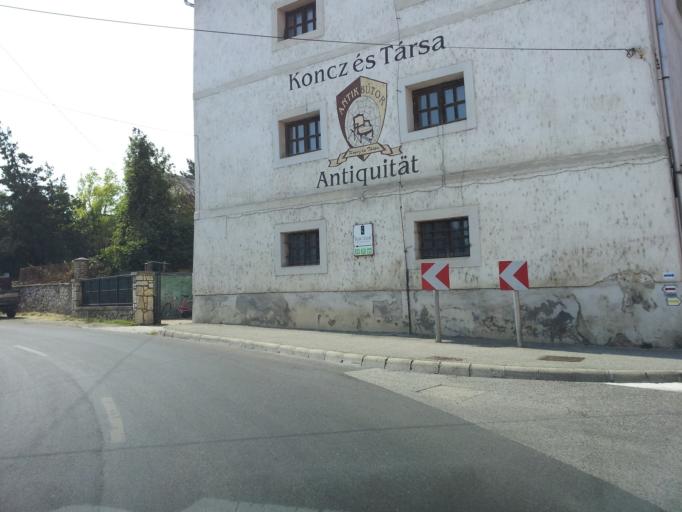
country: HU
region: Veszprem
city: Balatonfured
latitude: 46.9600
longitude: 17.8647
